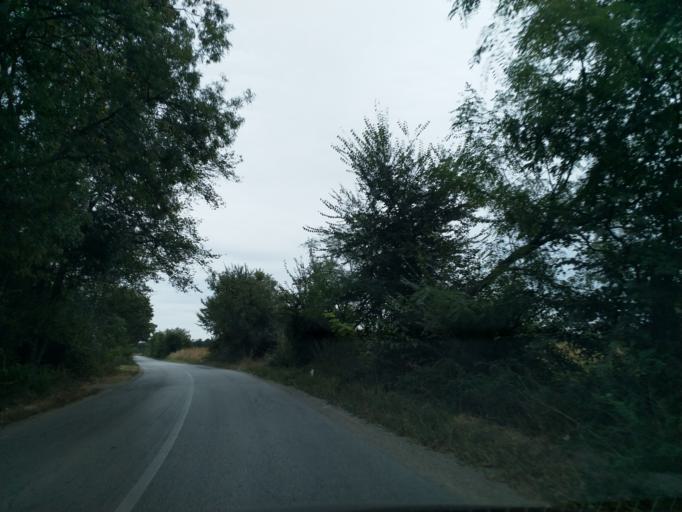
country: RS
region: Central Serbia
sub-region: Pomoravski Okrug
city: Paracin
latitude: 43.8387
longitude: 21.3724
